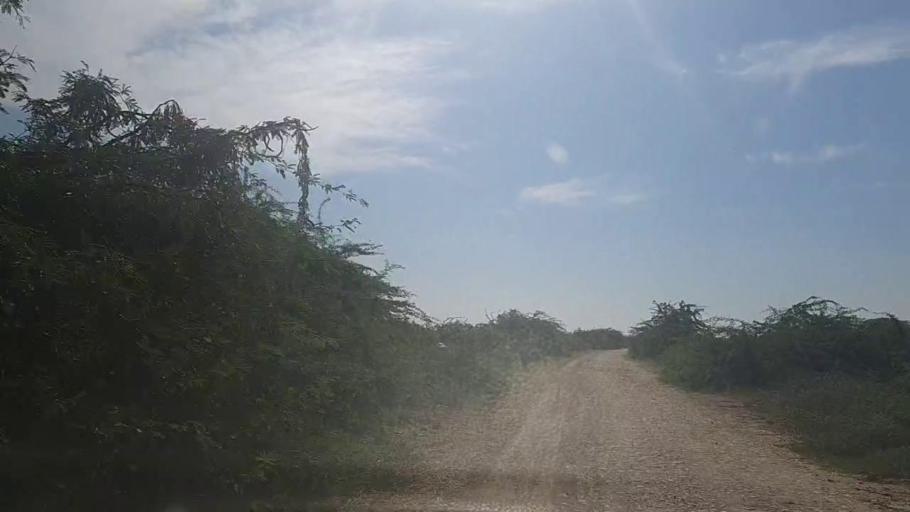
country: PK
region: Sindh
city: Mirpur Batoro
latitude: 24.6790
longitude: 68.1823
